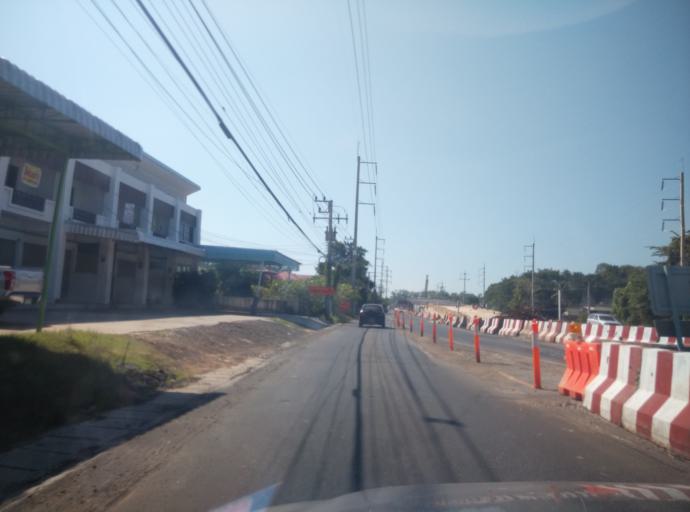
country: TH
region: Sisaket
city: Si Sa Ket
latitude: 15.1241
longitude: 104.2847
